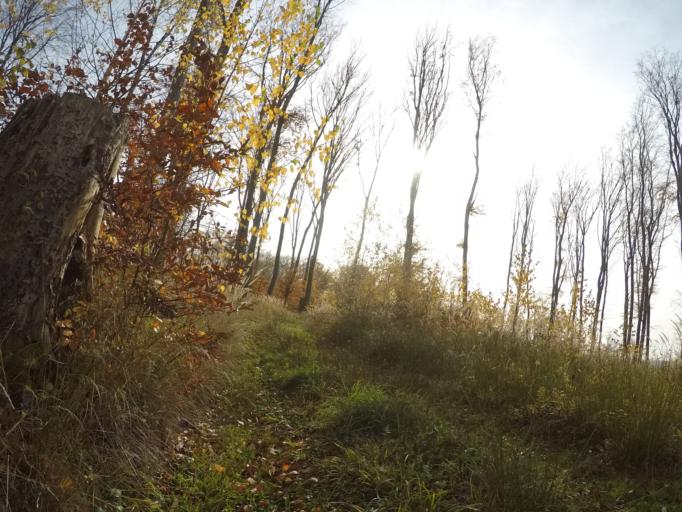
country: SK
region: Presovsky
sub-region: Okres Presov
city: Presov
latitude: 48.9508
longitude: 21.1868
